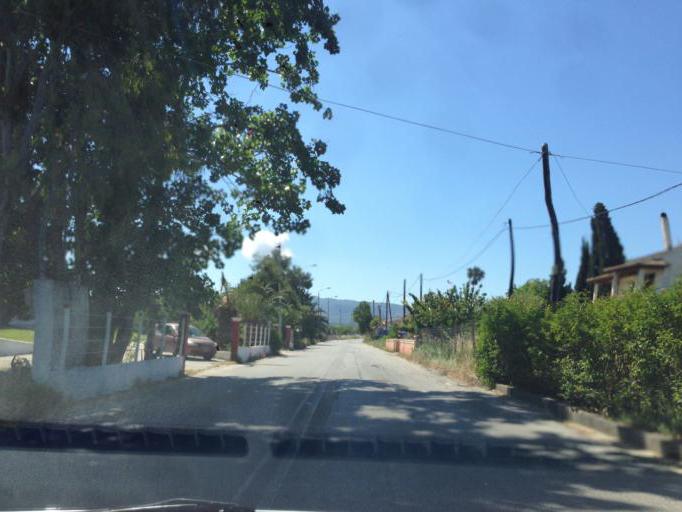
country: GR
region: Ionian Islands
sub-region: Nomos Kerkyras
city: Agios Georgis
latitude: 39.7770
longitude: 19.7108
